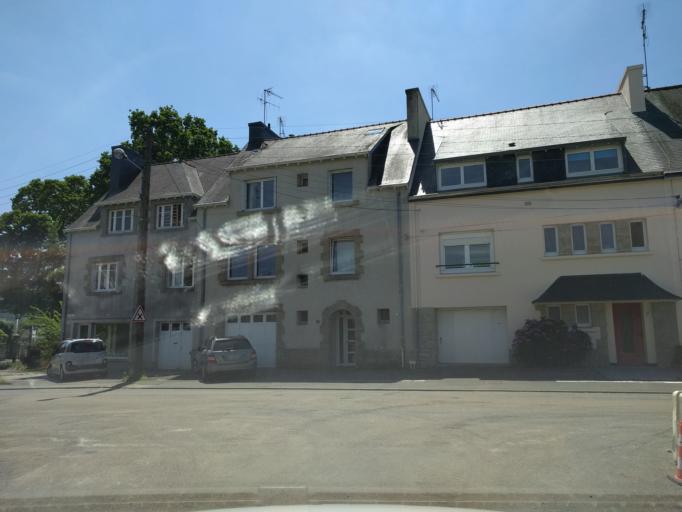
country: FR
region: Brittany
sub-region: Departement du Finistere
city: Quimper
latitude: 48.0036
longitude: -4.1095
